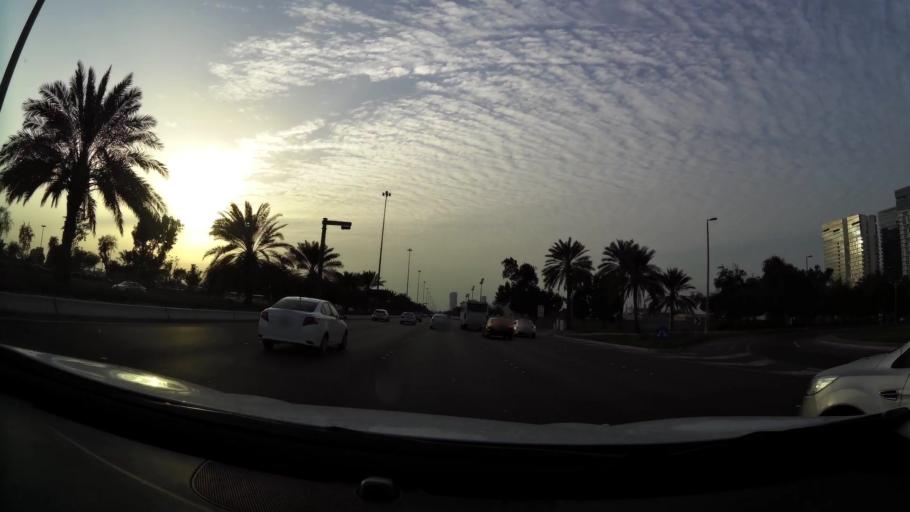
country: AE
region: Abu Dhabi
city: Abu Dhabi
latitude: 24.4099
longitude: 54.4633
